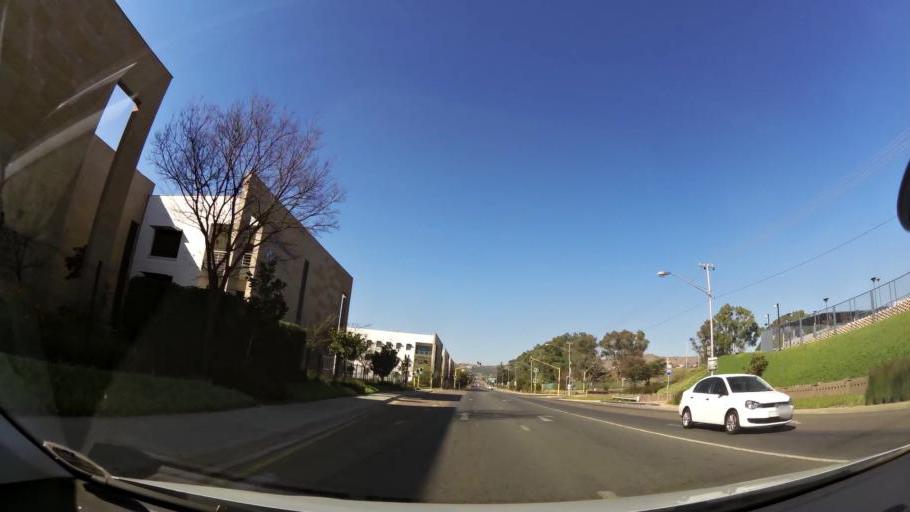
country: ZA
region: Gauteng
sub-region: City of Tshwane Metropolitan Municipality
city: Pretoria
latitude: -25.7661
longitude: 28.2214
